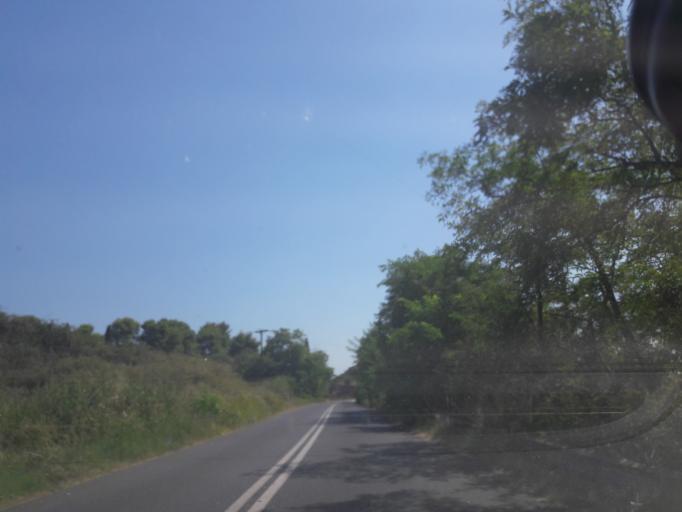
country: GR
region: Central Macedonia
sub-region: Nomos Chalkidikis
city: Nea Roda
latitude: 40.3679
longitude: 23.9176
